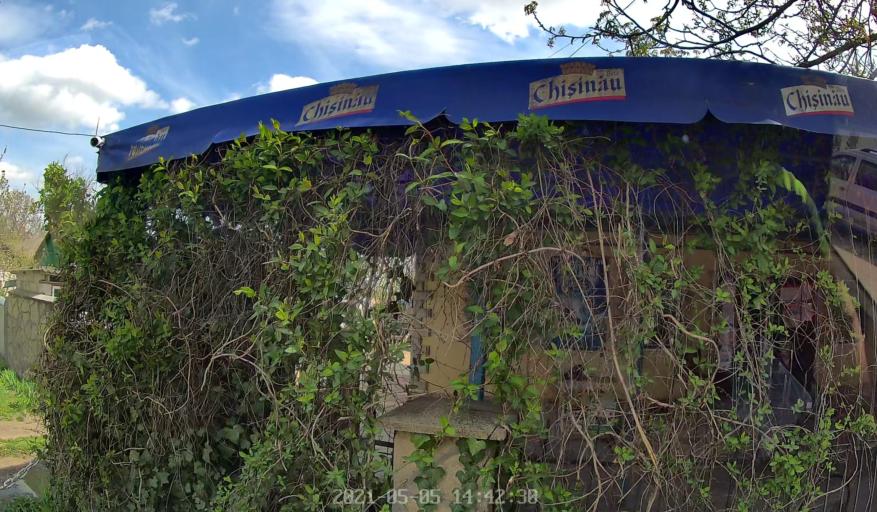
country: MD
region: Chisinau
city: Vadul lui Voda
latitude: 47.0914
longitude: 29.1746
